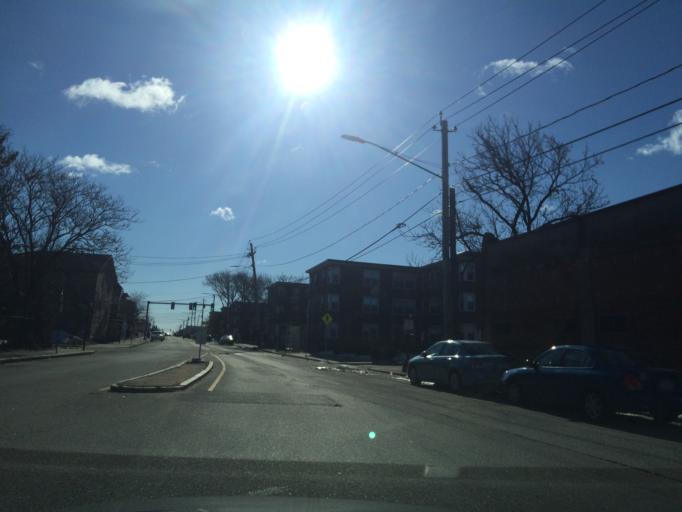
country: US
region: Massachusetts
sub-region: Middlesex County
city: Watertown
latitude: 42.3574
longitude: -71.1537
